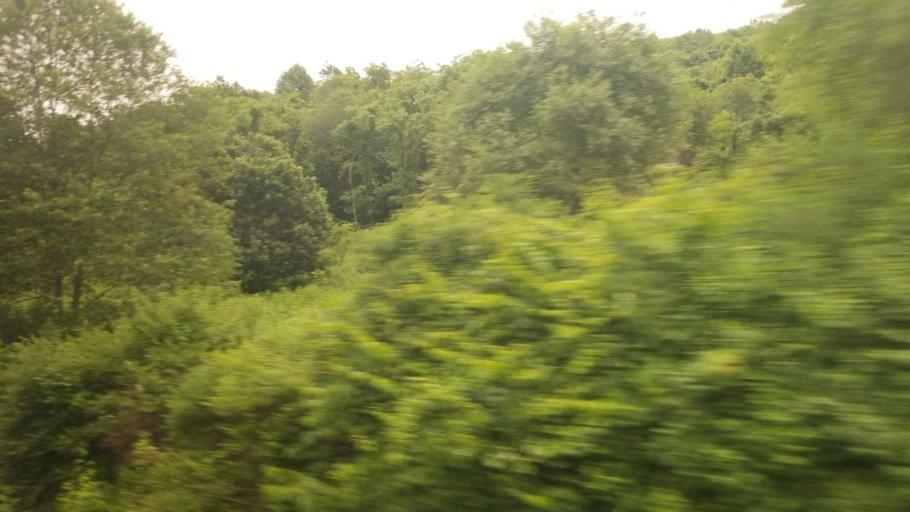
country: US
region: Pennsylvania
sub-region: Somerset County
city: Milford
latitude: 39.8276
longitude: -79.3112
